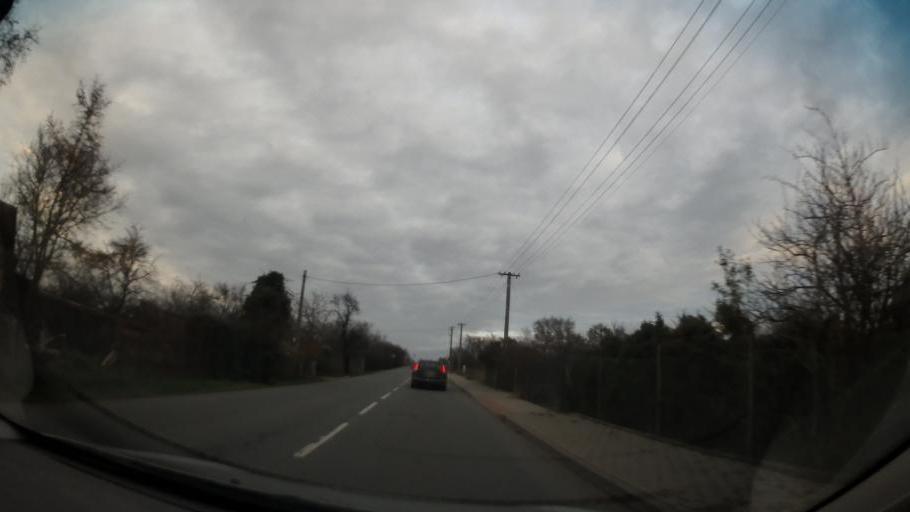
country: CZ
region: South Moravian
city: Oslavany
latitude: 49.1328
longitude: 16.3551
